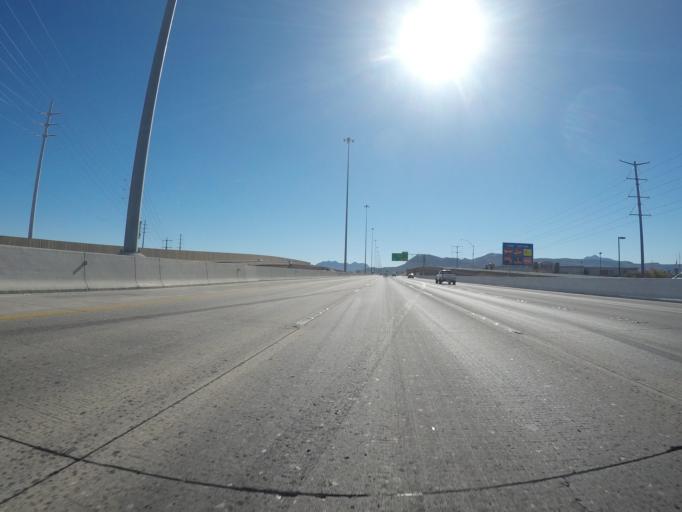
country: US
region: Nevada
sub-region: Clark County
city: Whitney
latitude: 36.0692
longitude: -115.0353
